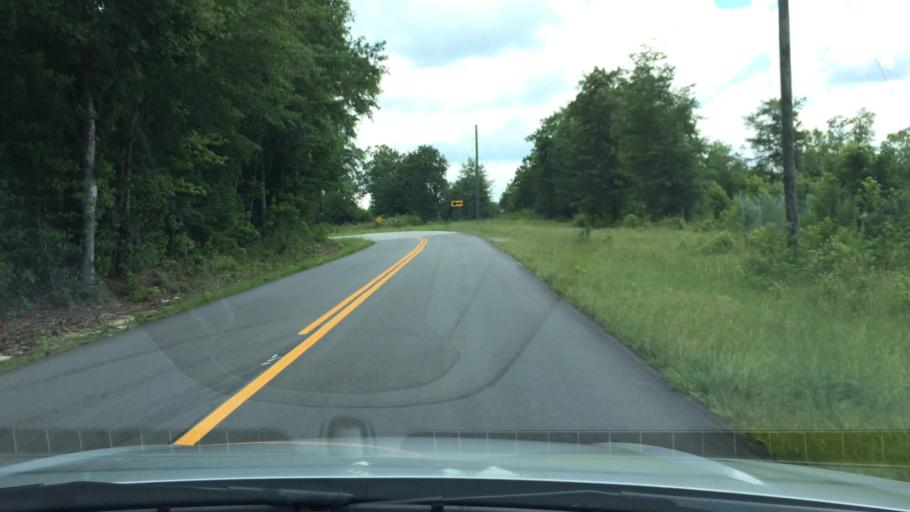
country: US
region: South Carolina
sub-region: Calhoun County
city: Oak Grove
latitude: 33.8077
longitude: -81.0090
